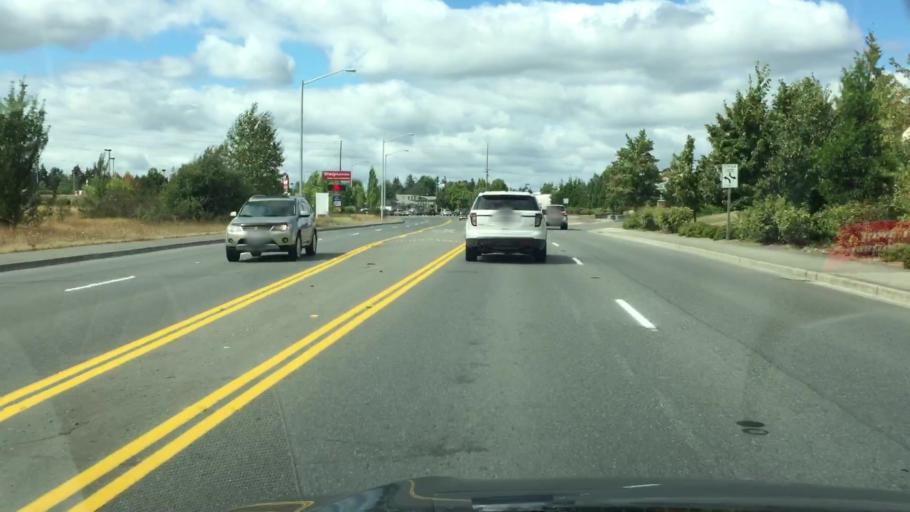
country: US
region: Washington
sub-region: Pierce County
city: Graham
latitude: 47.0978
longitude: -122.2900
